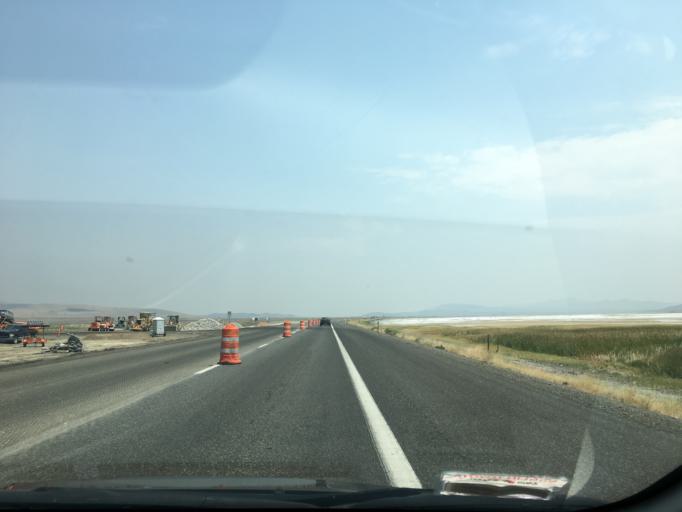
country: US
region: Nevada
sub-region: Lyon County
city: Fernley
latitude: 39.7026
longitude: -119.0991
